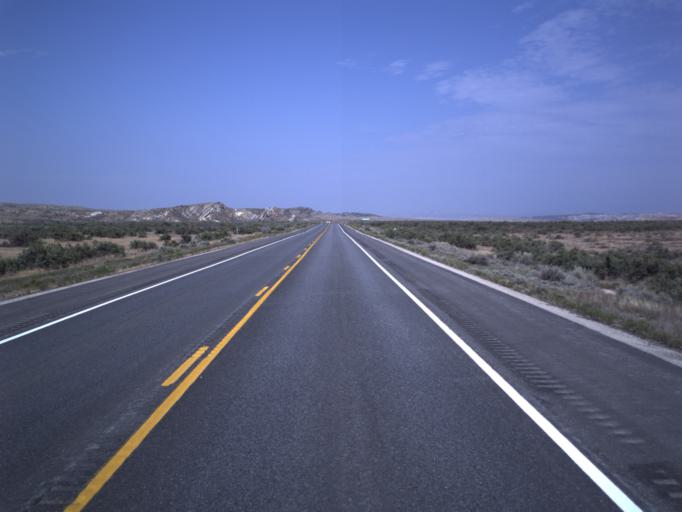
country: US
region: Utah
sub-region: Uintah County
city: Naples
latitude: 40.2868
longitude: -109.1377
